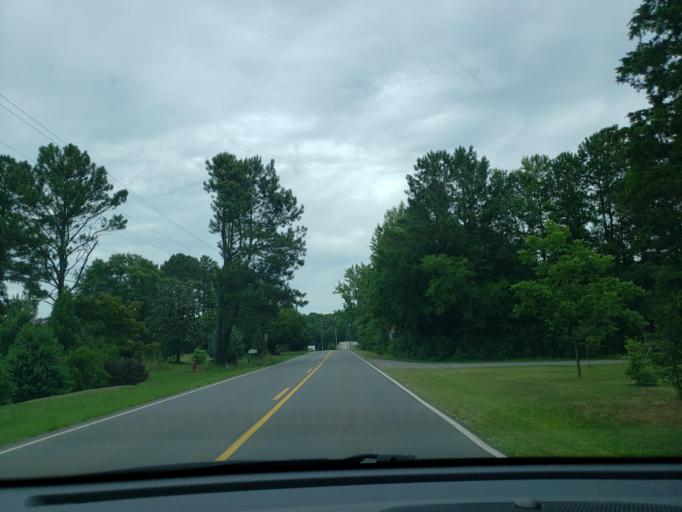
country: US
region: North Carolina
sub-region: Wake County
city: Green Level
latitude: 35.7346
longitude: -79.0009
